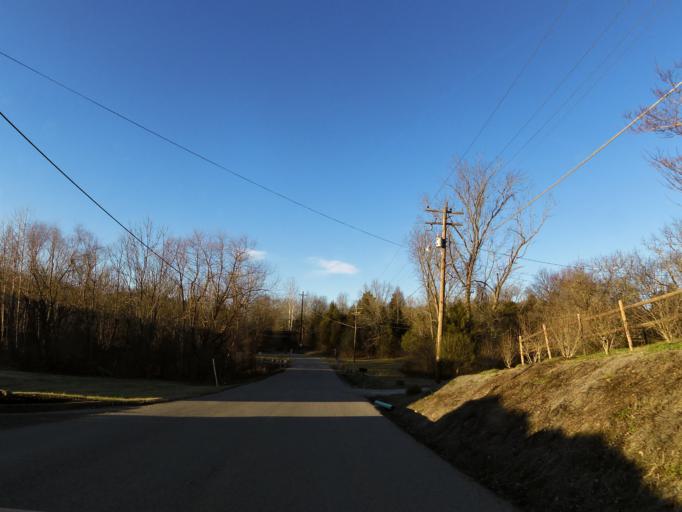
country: US
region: Tennessee
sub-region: Sevier County
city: Seymour
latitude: 35.9188
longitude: -83.8245
